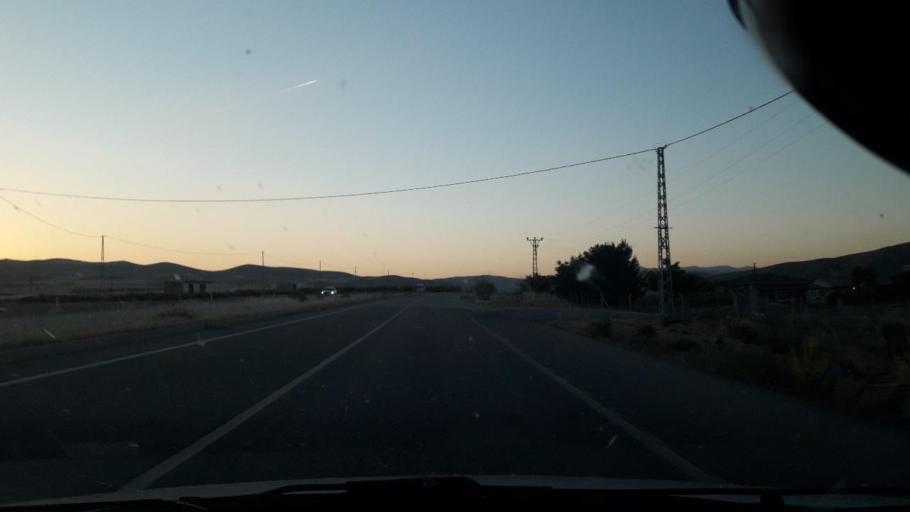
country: TR
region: Malatya
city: Yazihan
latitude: 38.6113
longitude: 38.1743
